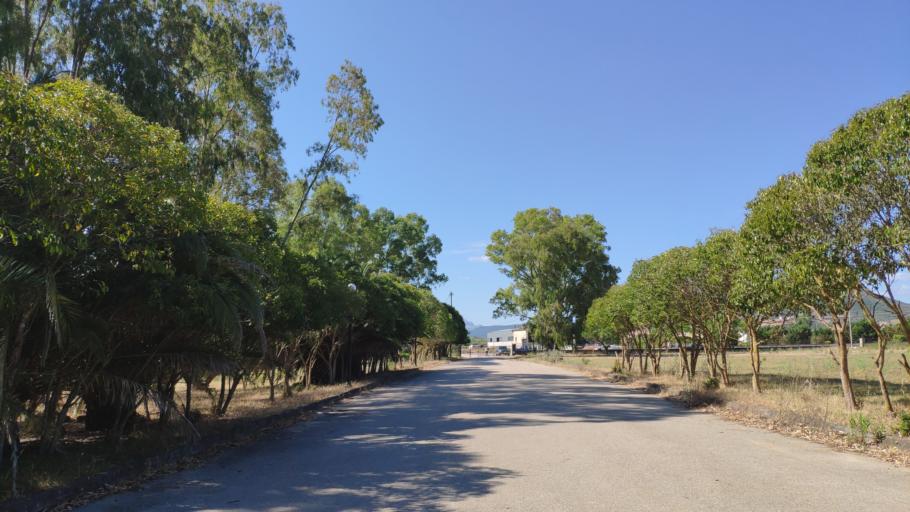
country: GR
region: West Greece
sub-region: Nomos Aitolias kai Akarnanias
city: Vonitsa
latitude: 38.9208
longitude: 20.9002
